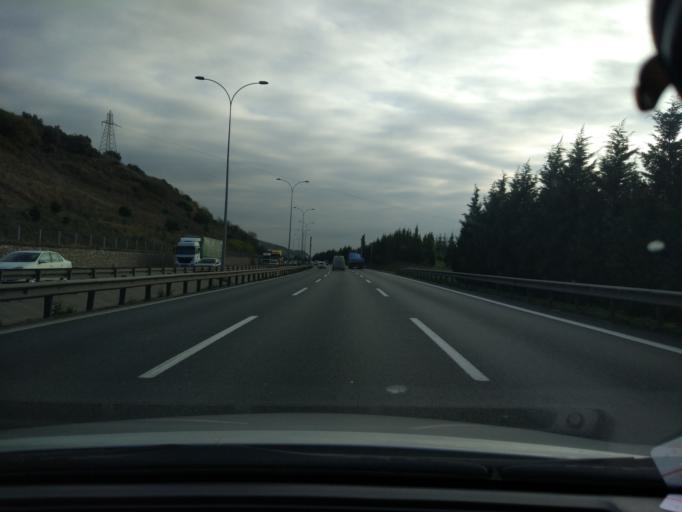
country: TR
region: Kocaeli
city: Ulasli
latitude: 40.7792
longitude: 29.7014
